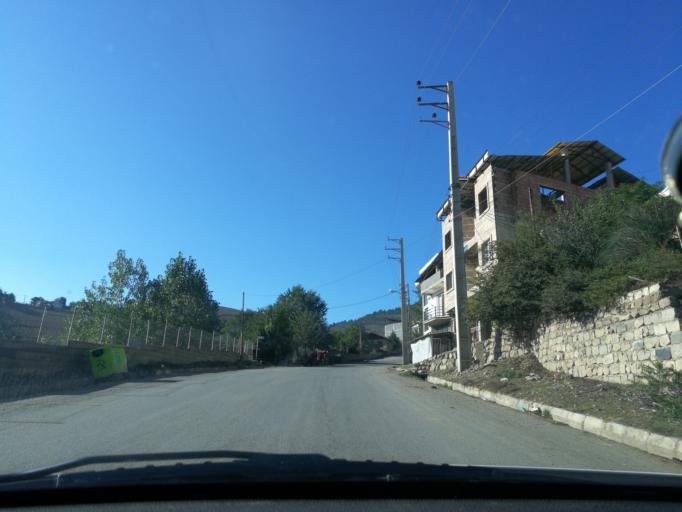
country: IR
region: Mazandaran
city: `Abbasabad
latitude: 36.5507
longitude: 51.1897
